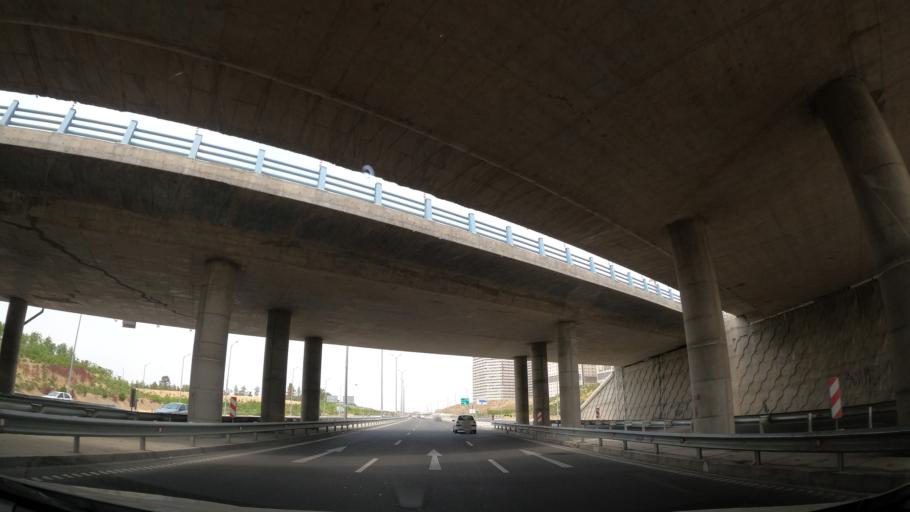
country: IR
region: Tehran
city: Shahr-e Qods
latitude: 35.7458
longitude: 51.1905
